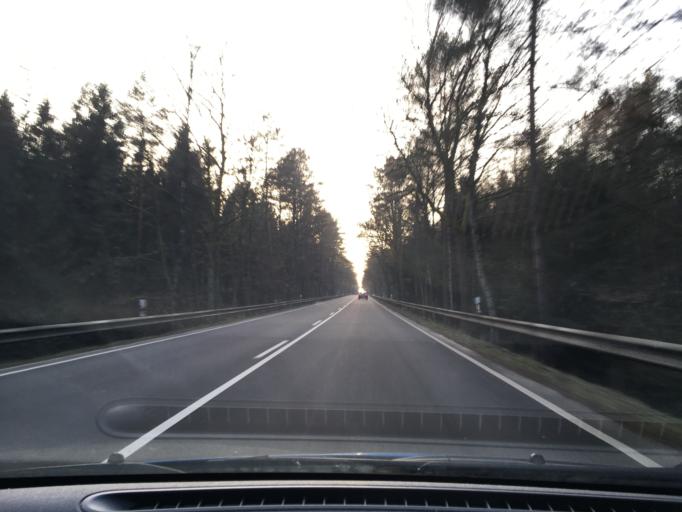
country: DE
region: Lower Saxony
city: Sprakensehl
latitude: 52.8000
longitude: 10.4056
